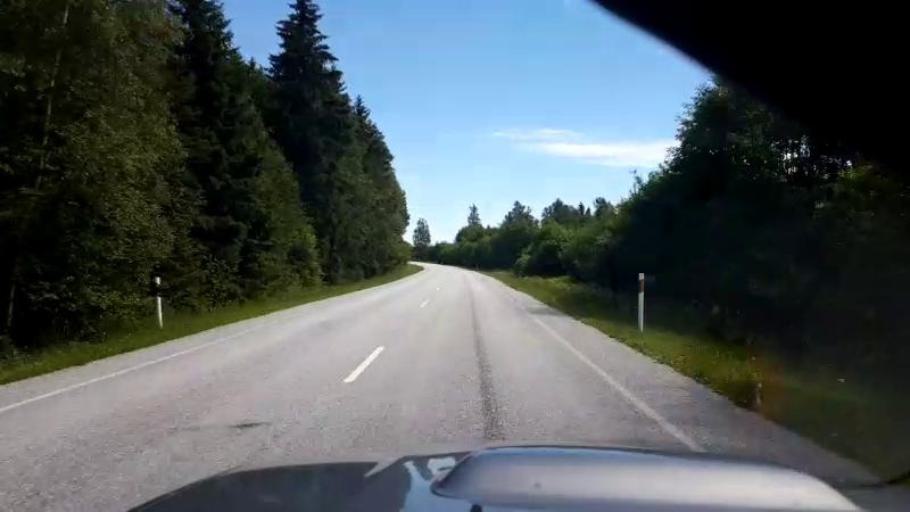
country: EE
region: Laeaene-Virumaa
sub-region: Rakke vald
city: Rakke
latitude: 58.9210
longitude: 26.2454
